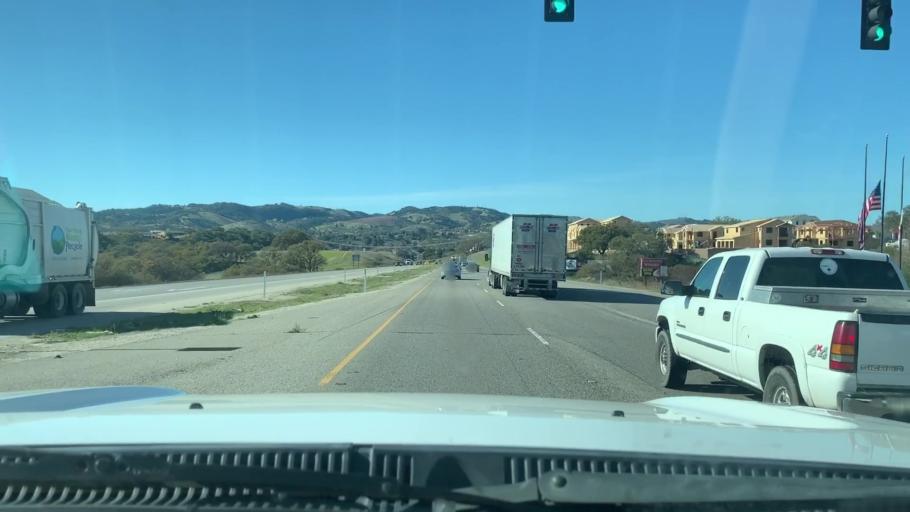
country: US
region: California
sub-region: San Luis Obispo County
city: Paso Robles
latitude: 35.6446
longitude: -120.6724
